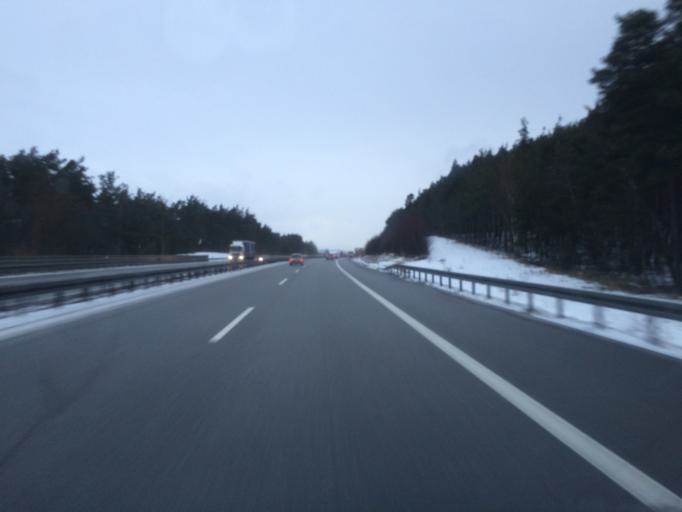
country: DE
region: Bavaria
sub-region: Upper Palatinate
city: Maxhutte-Haidhof
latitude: 49.1948
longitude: 12.1177
